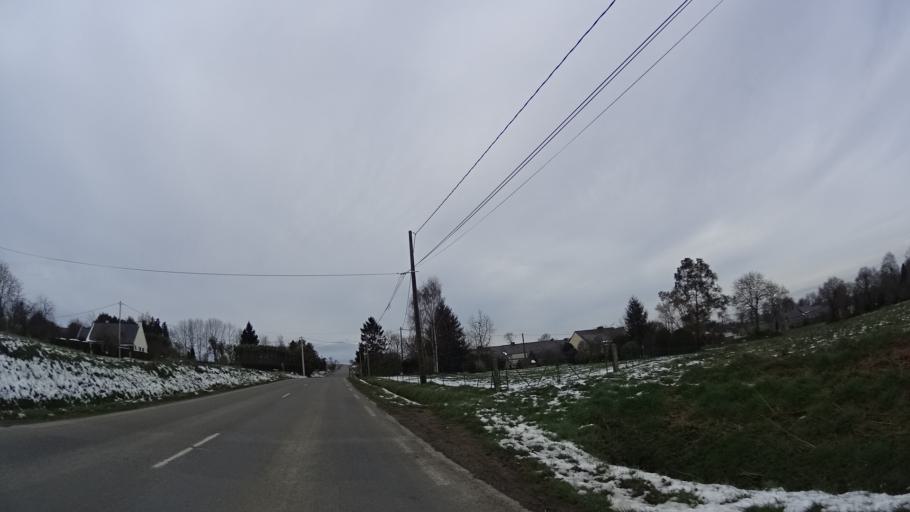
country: FR
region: Brittany
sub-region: Departement des Cotes-d'Armor
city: Plouasne
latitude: 48.3108
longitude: -1.9503
